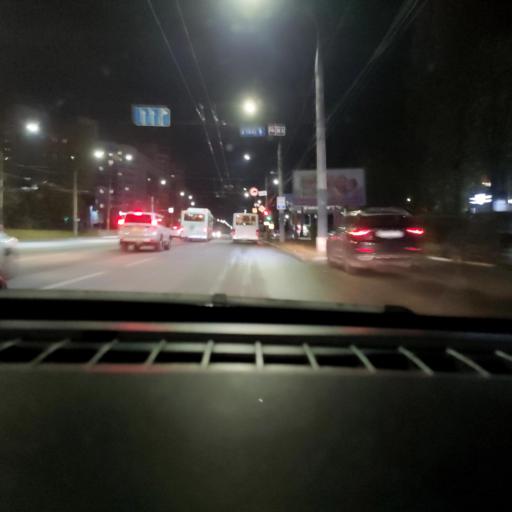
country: RU
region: Voronezj
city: Voronezh
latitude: 51.6660
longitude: 39.2491
